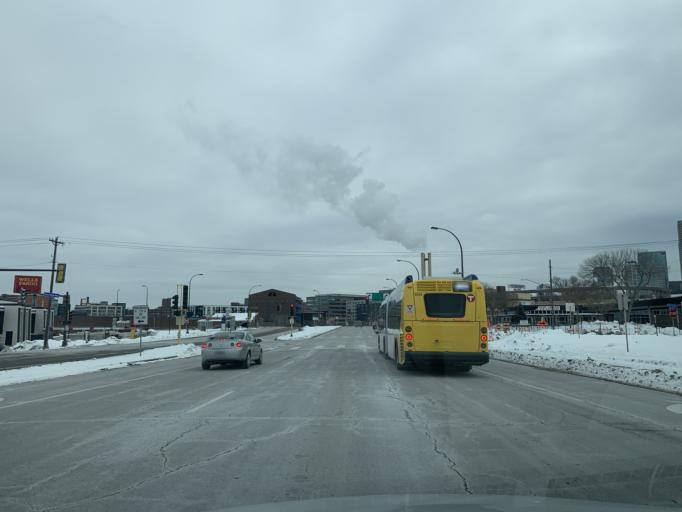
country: US
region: Minnesota
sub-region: Hennepin County
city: Minneapolis
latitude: 44.9843
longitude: -93.2864
